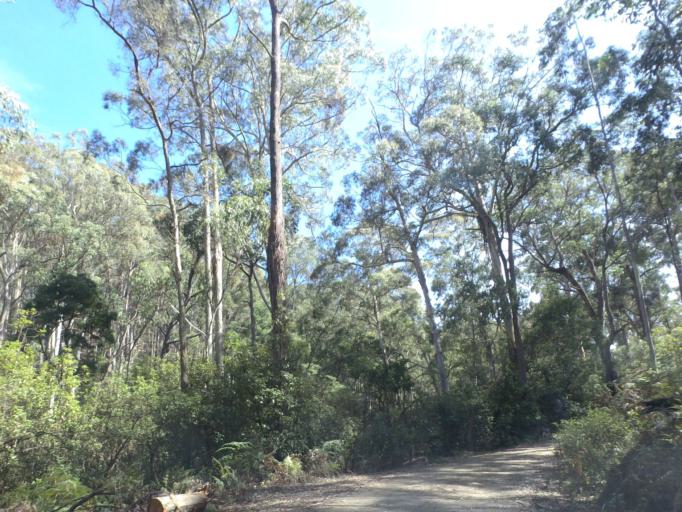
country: AU
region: Victoria
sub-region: Moorabool
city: Bacchus Marsh
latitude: -37.4500
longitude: 144.2625
